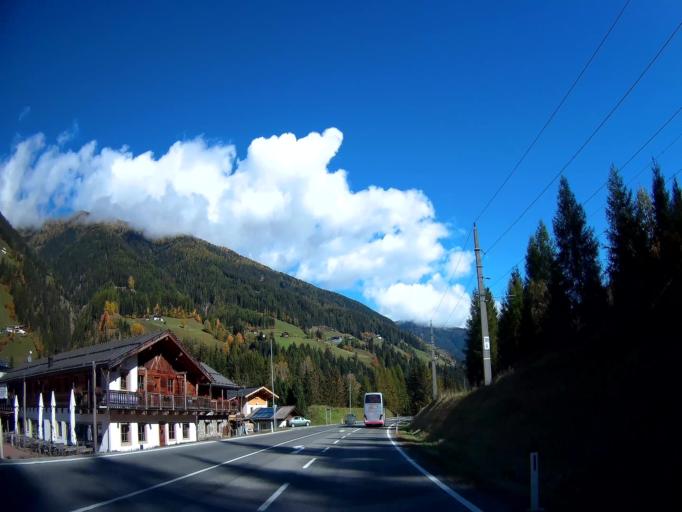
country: AT
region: Tyrol
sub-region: Politischer Bezirk Lienz
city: Sillian
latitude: 46.7425
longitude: 12.3856
